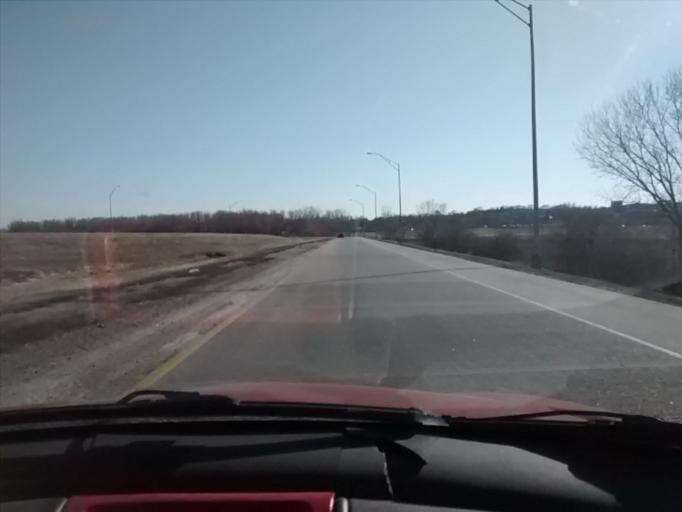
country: US
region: Nebraska
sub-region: Sarpy County
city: Offutt Air Force Base
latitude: 41.1434
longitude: -95.9393
